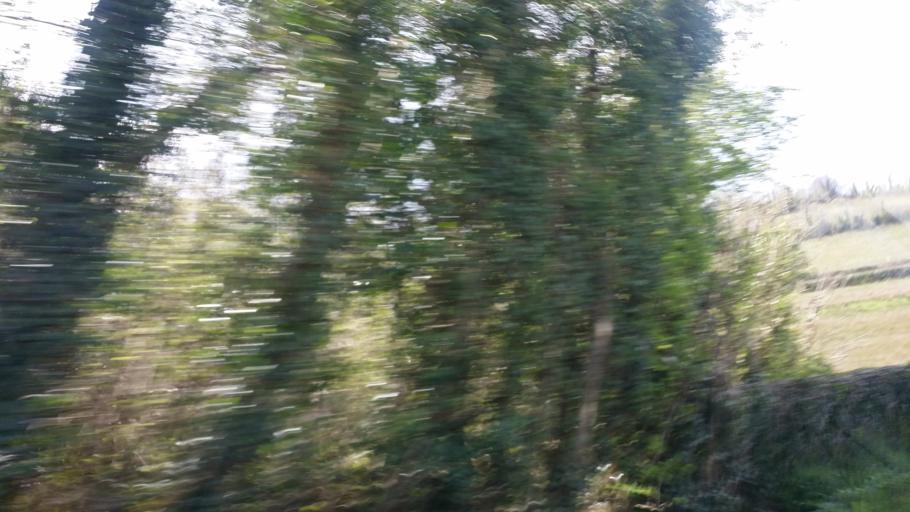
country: GB
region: Northern Ireland
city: Irvinestown
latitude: 54.4574
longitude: -7.8263
